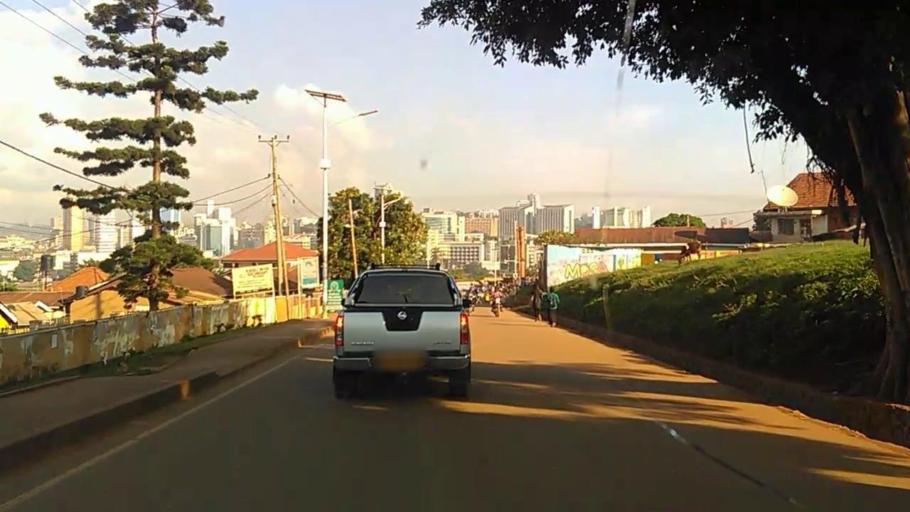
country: UG
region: Central Region
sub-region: Kampala District
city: Kampala
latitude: 0.3088
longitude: 32.5943
